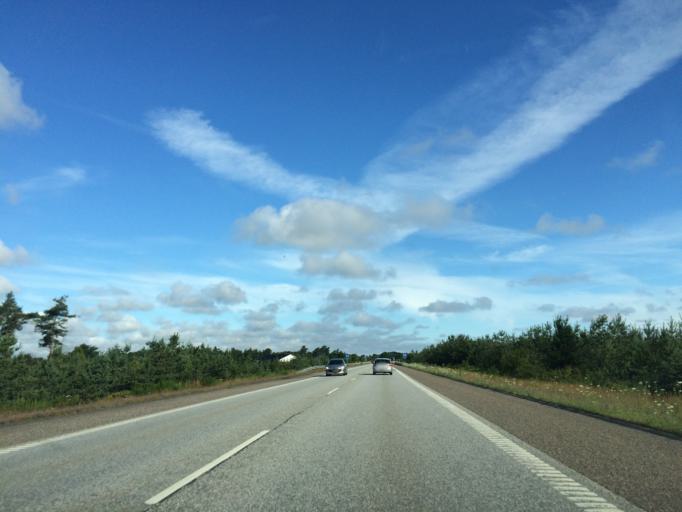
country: DK
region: Central Jutland
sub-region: Viborg Kommune
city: Viborg
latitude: 56.3861
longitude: 9.4503
